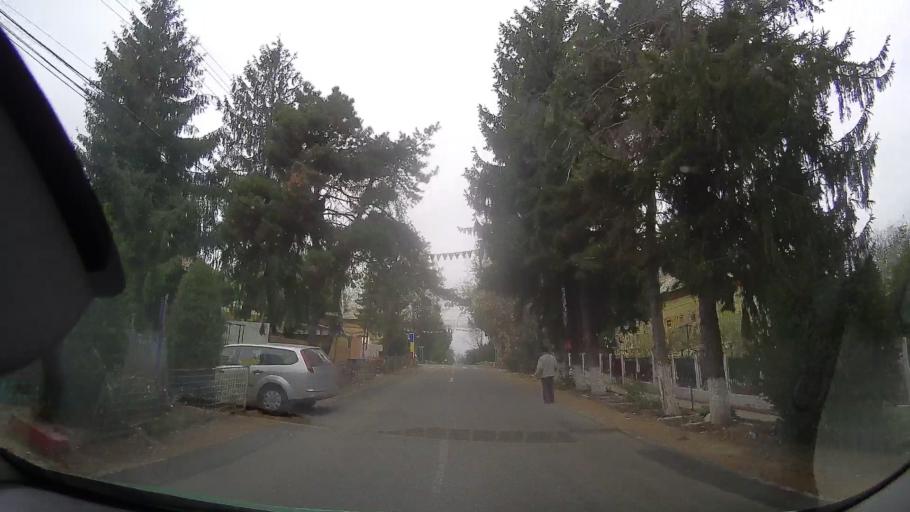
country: RO
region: Buzau
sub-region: Comuna Bradeanu
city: Bradeanu
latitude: 44.9253
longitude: 26.8623
